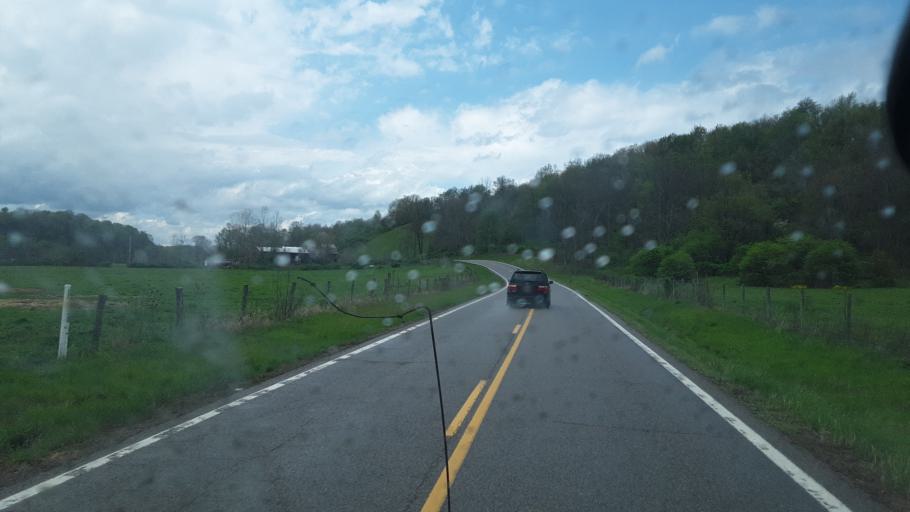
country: US
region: Ohio
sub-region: Guernsey County
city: Mantua
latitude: 40.0802
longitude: -81.7623
